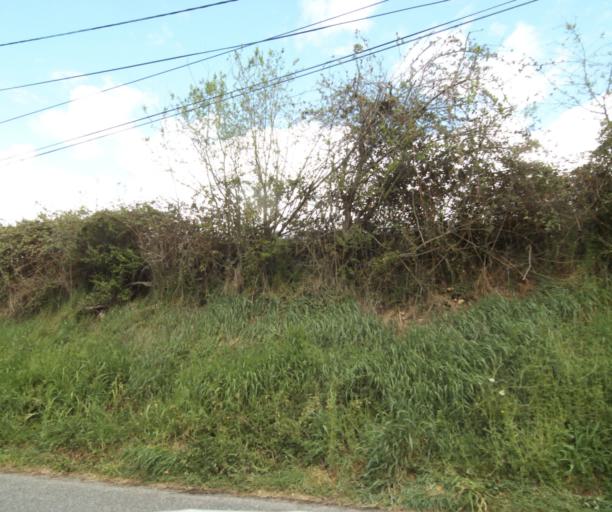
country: FR
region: Midi-Pyrenees
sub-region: Departement de l'Ariege
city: Saverdun
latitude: 43.2310
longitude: 1.5797
